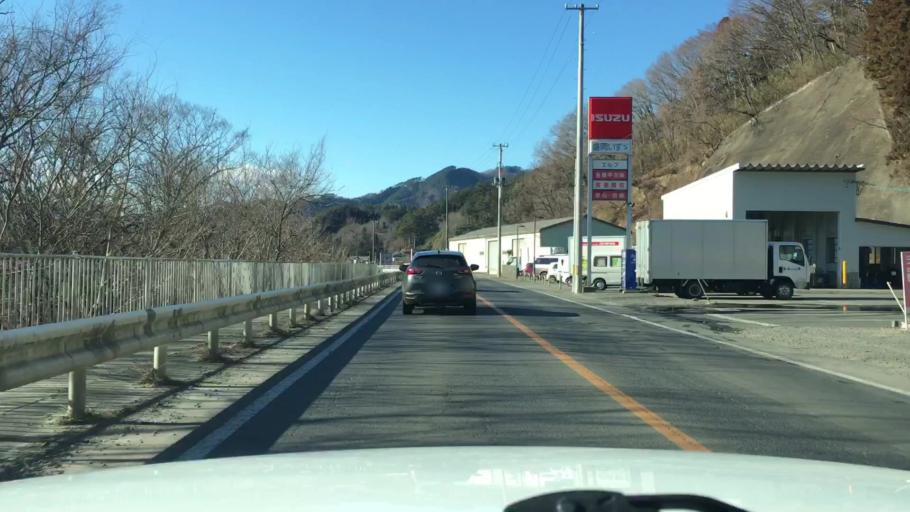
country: JP
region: Iwate
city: Miyako
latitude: 39.6324
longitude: 141.9020
